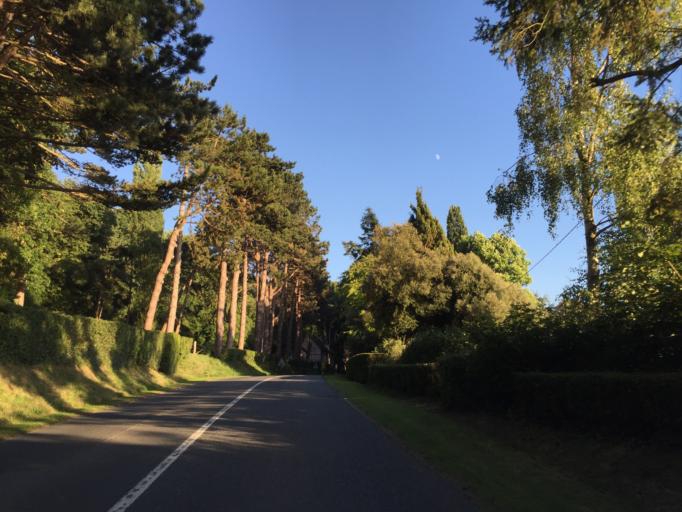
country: FR
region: Lower Normandy
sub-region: Departement du Calvados
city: Equemauville
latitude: 49.4055
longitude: 0.1782
